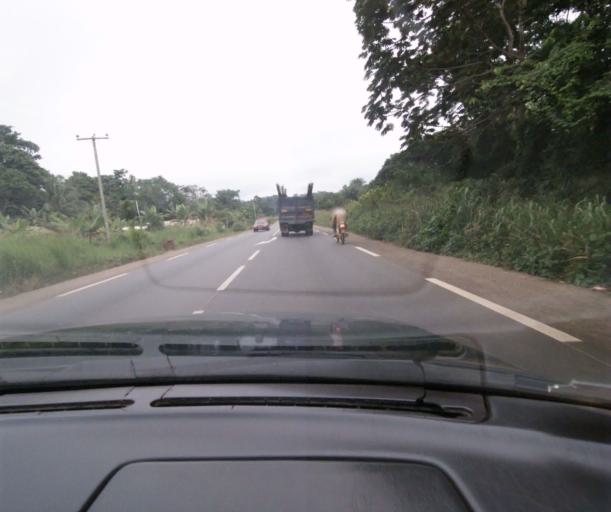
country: CM
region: Centre
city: Obala
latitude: 4.2108
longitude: 11.4435
